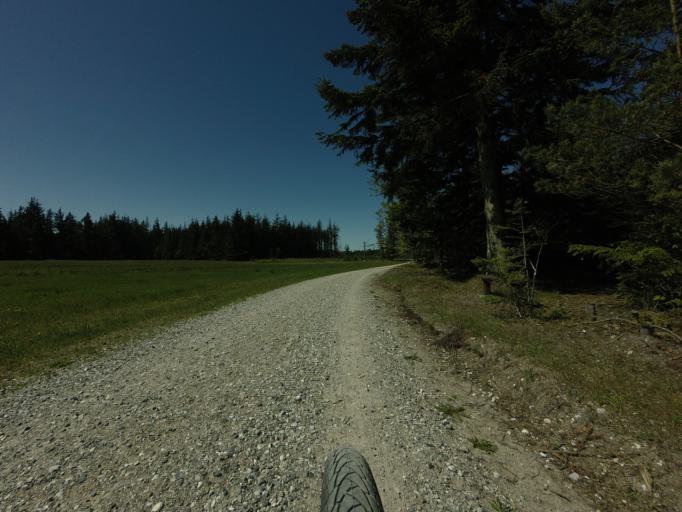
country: DK
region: North Denmark
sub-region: Jammerbugt Kommune
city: Pandrup
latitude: 57.2422
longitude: 9.5933
